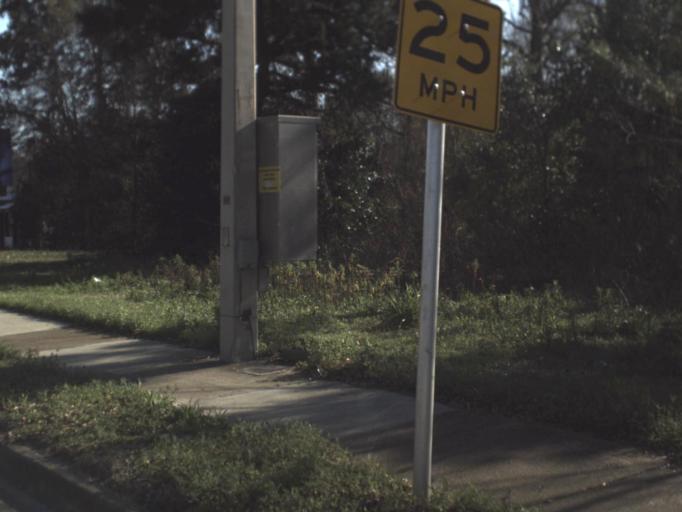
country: US
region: Florida
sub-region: Jackson County
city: Marianna
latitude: 30.7775
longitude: -85.2365
